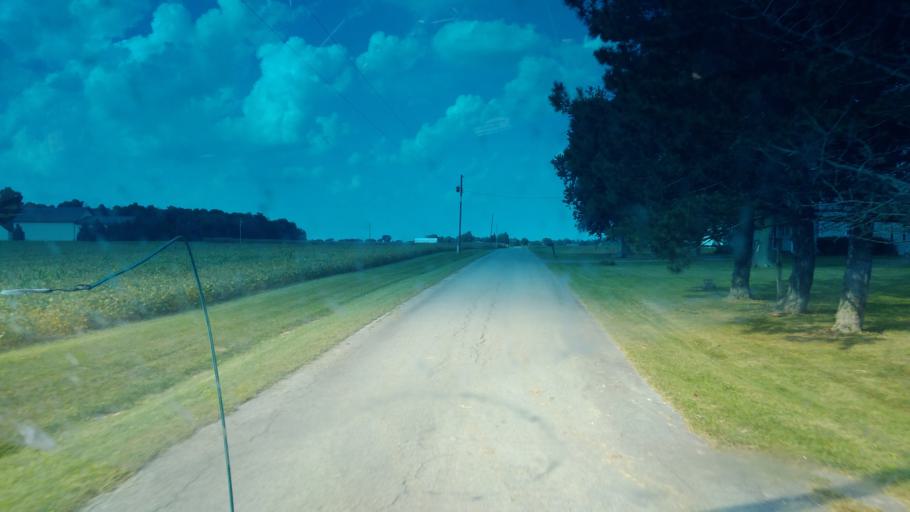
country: US
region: Ohio
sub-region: Hardin County
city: Forest
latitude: 40.8493
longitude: -83.5761
